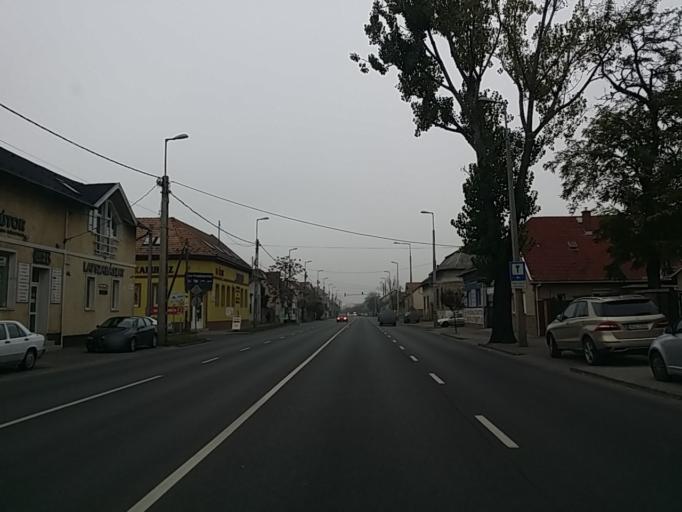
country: HU
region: Budapest
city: Budapest XV. keruelet
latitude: 47.5574
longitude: 19.1254
